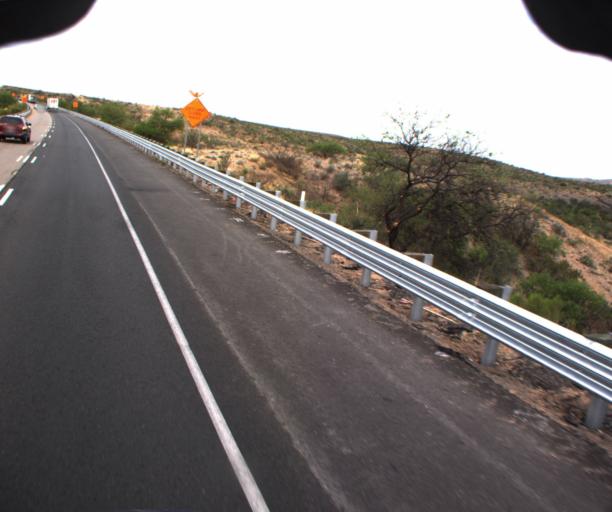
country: US
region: Arizona
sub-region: Pima County
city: Vail
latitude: 31.9989
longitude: -110.6296
